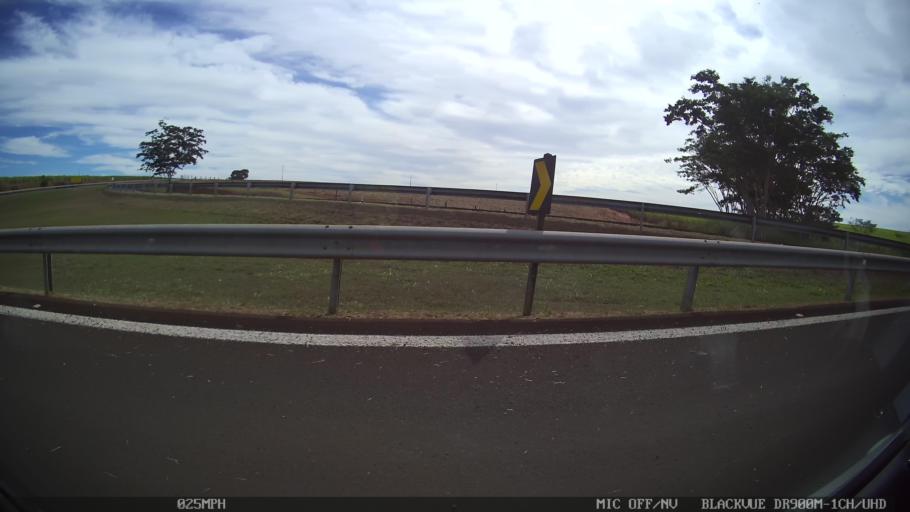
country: BR
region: Sao Paulo
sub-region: Taquaritinga
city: Taquaritinga
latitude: -21.5144
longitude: -48.5410
